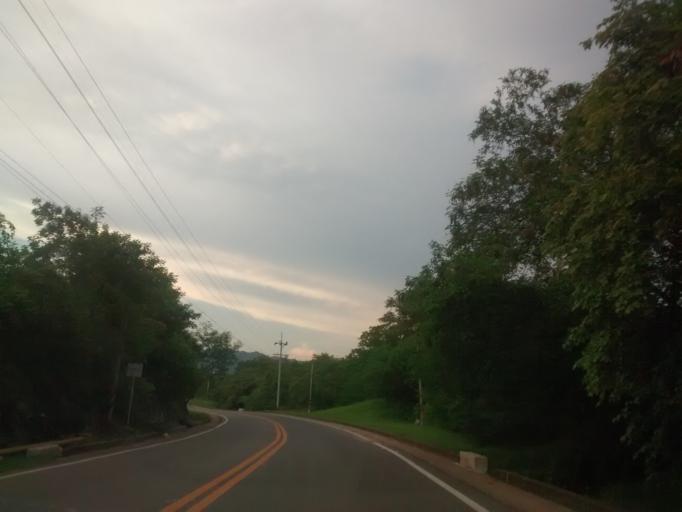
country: CO
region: Cundinamarca
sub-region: Girardot
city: Girardot City
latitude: 4.3363
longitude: -74.8049
